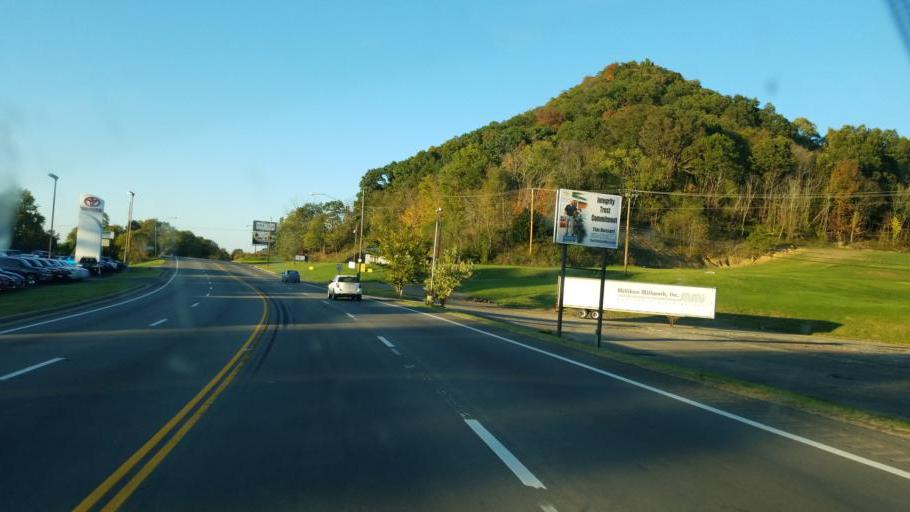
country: US
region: Ohio
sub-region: Scioto County
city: Rosemount
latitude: 38.7692
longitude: -82.9857
